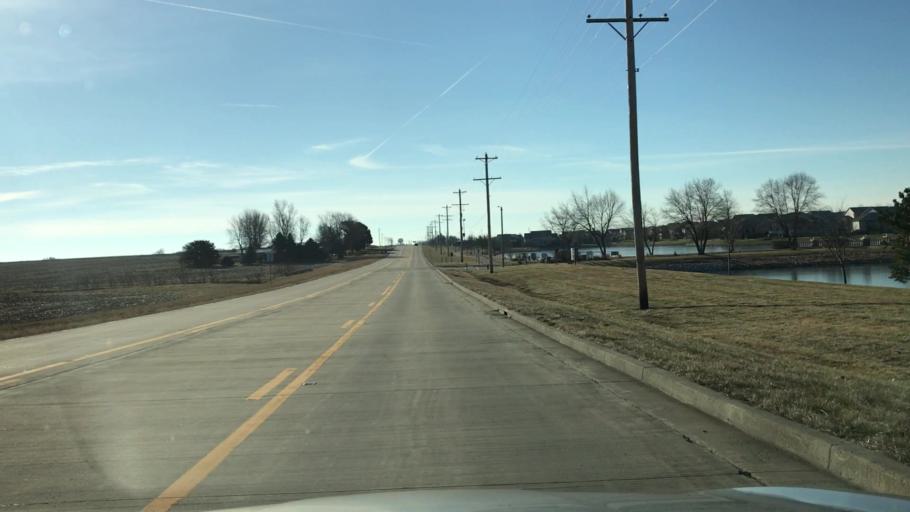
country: US
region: Illinois
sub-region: McLean County
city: Normal
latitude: 40.5582
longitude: -88.9446
